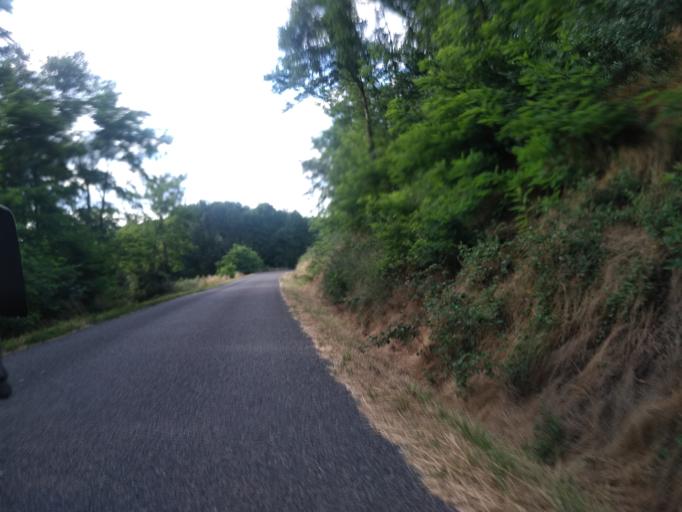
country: FR
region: Rhone-Alpes
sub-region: Departement du Rhone
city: Haute-Rivoire
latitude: 45.7269
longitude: 4.3492
